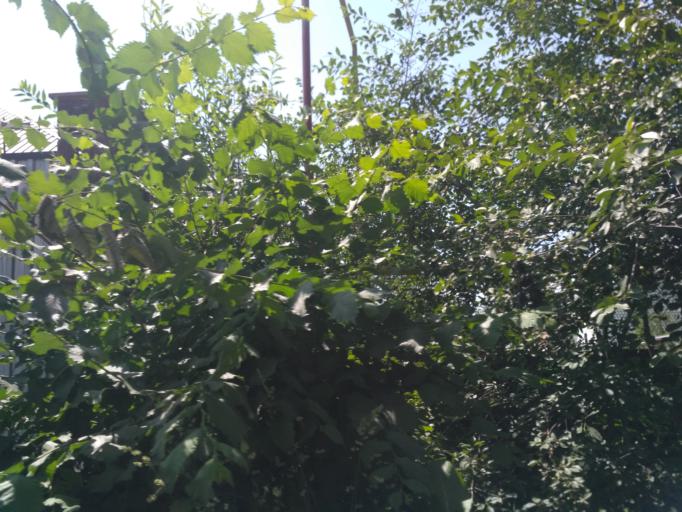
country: KZ
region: Almaty Oblysy
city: Burunday
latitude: 43.1904
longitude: 76.6190
